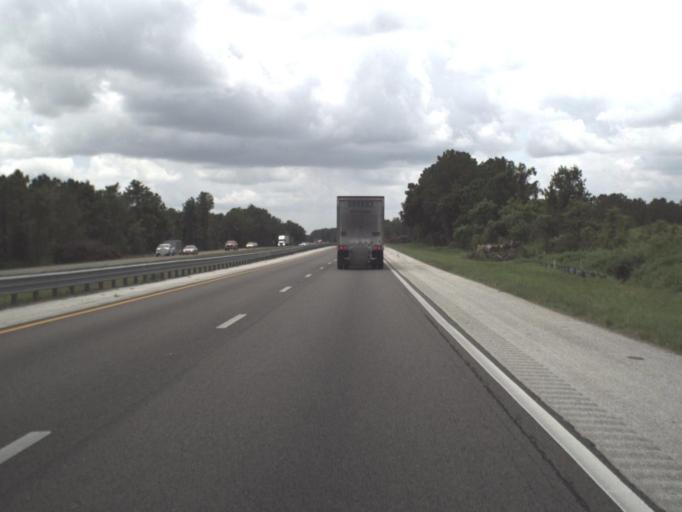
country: US
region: Florida
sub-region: Pasco County
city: Wesley Chapel
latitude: 28.2613
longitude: -82.3341
